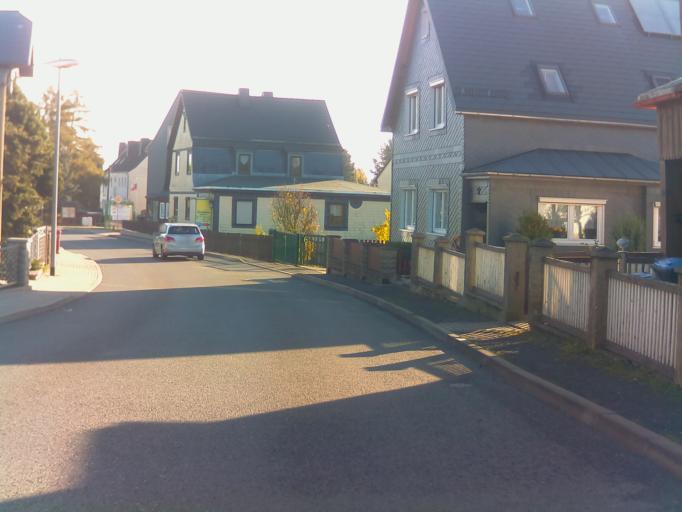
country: DE
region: Thuringia
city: Schmiedefeld
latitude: 50.5310
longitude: 11.2155
